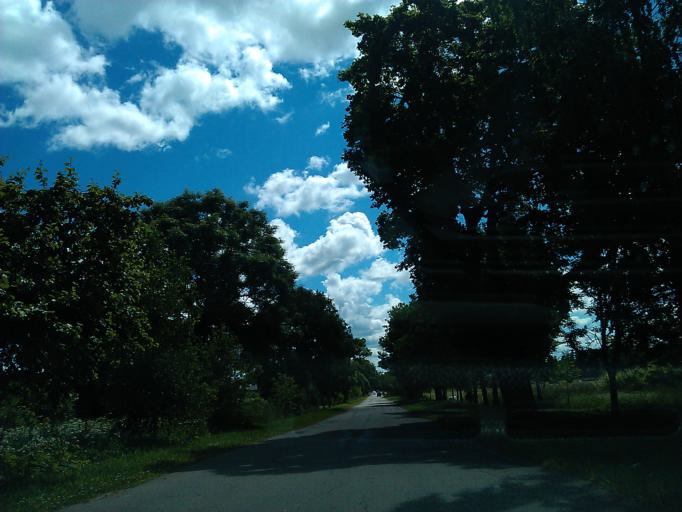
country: LV
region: Varaklani
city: Varaklani
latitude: 56.6072
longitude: 26.7666
